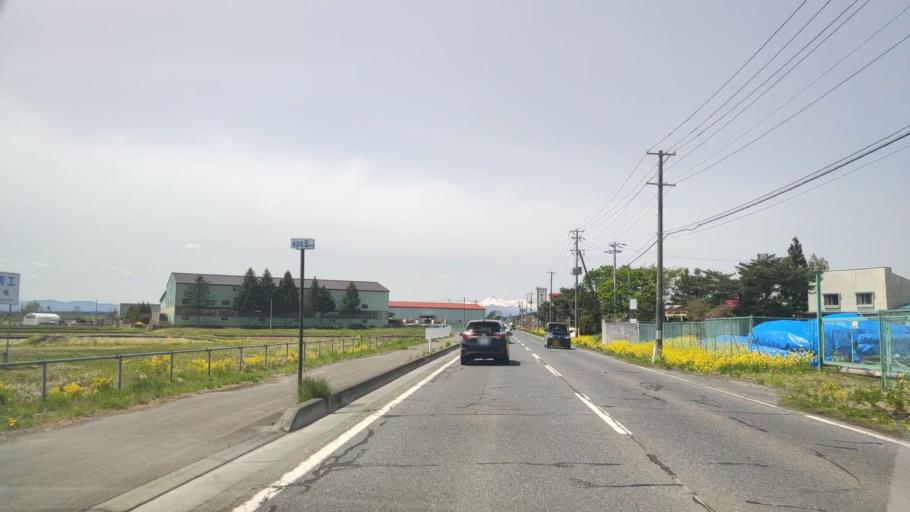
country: JP
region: Aomori
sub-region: Misawa Shi
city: Inuotose
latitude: 40.6116
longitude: 141.2668
